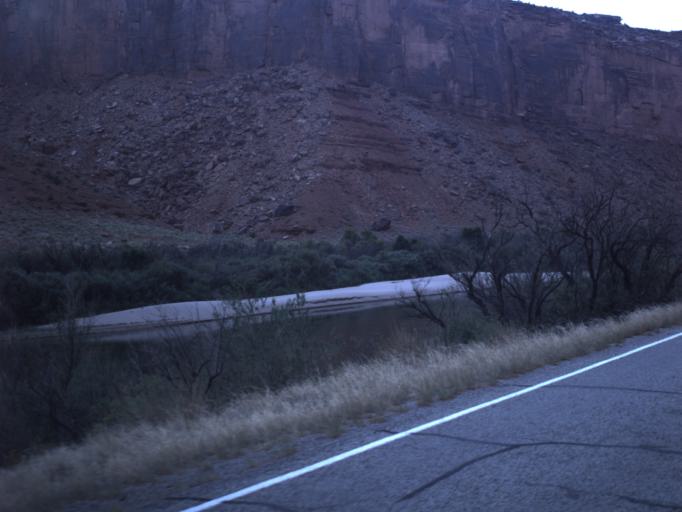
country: US
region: Utah
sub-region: Grand County
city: Moab
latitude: 38.7916
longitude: -109.3360
